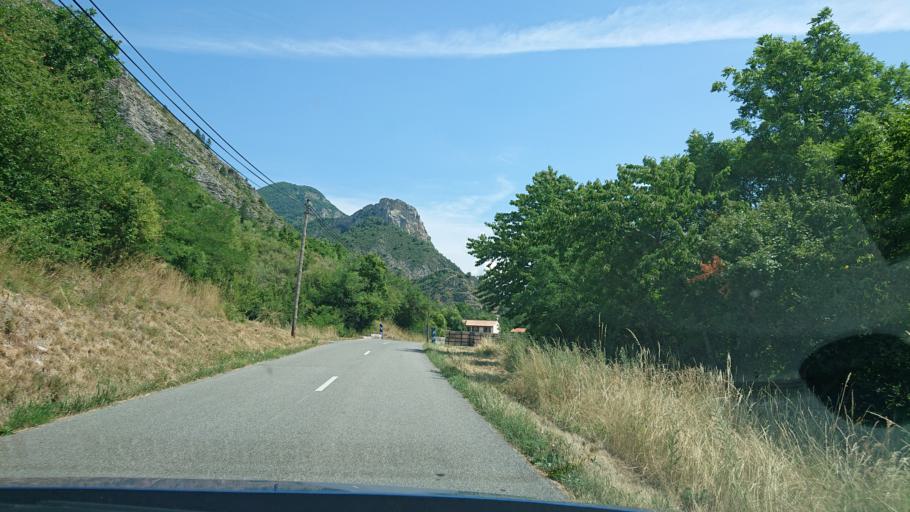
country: FR
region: Provence-Alpes-Cote d'Azur
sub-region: Departement des Hautes-Alpes
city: Tallard
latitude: 44.3661
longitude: 6.0555
